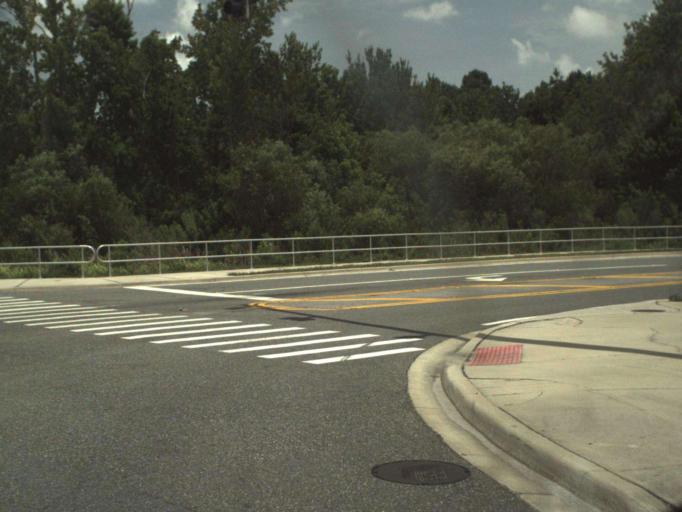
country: US
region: Florida
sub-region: Seminole County
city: Oviedo
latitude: 28.6614
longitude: -81.2243
